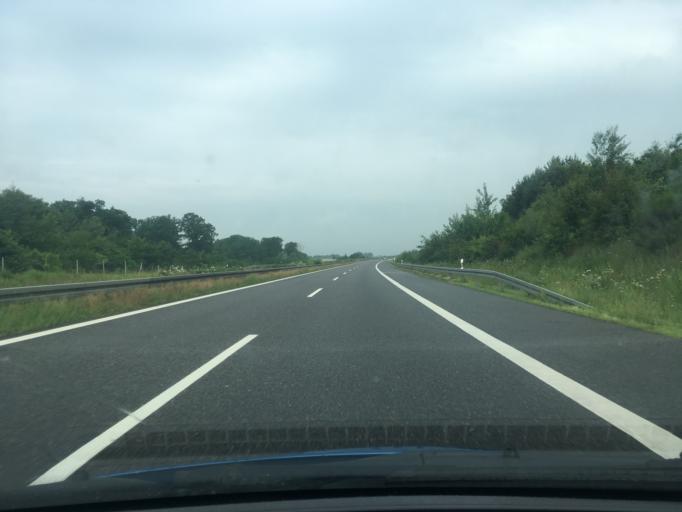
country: DE
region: Mecklenburg-Vorpommern
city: Tessin
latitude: 54.0079
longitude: 12.5254
